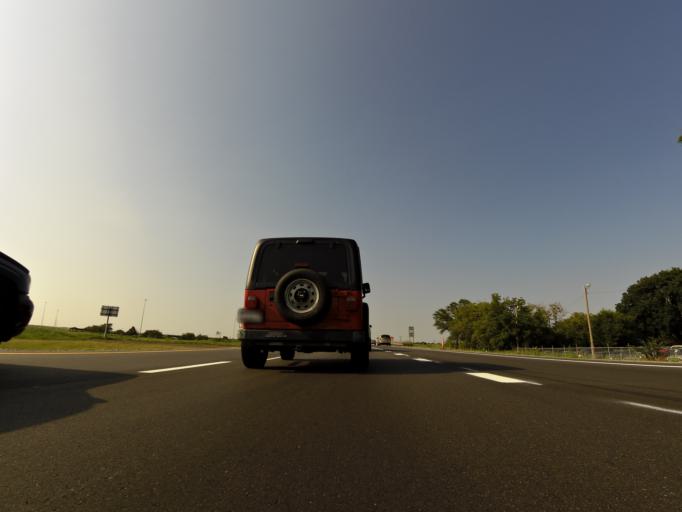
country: US
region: Kansas
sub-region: Sedgwick County
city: Park City
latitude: 37.7560
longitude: -97.3200
